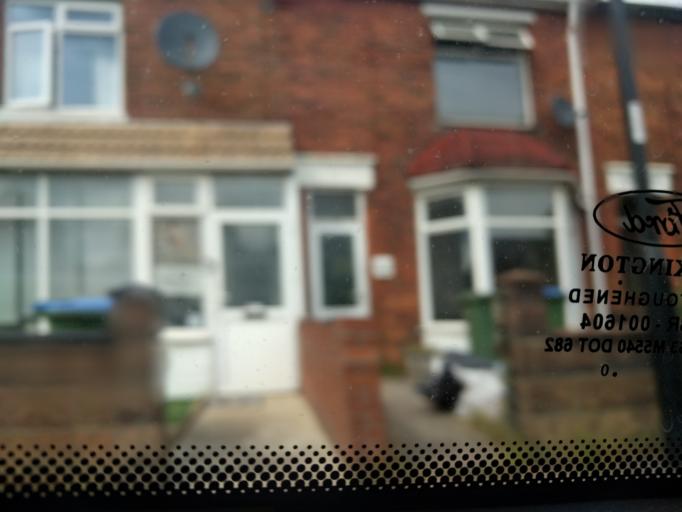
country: GB
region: England
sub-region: Southampton
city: Southampton
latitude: 50.9263
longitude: -1.4370
